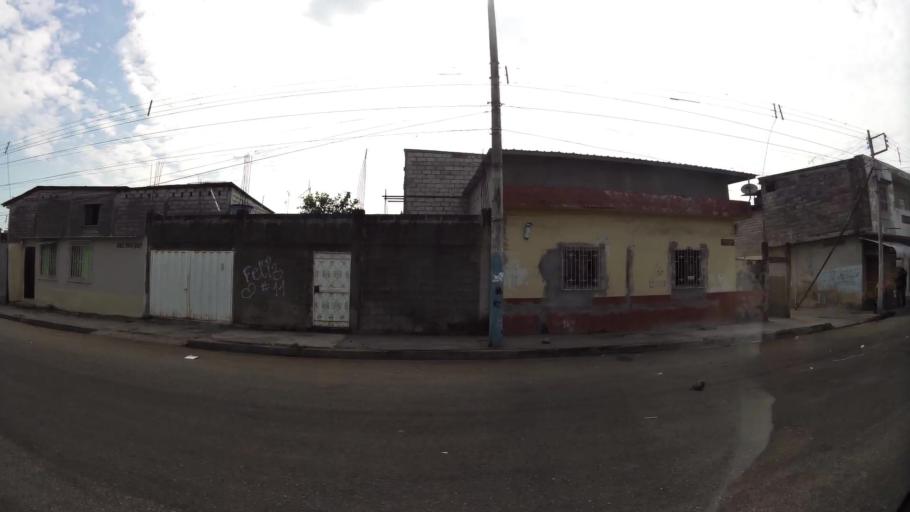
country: EC
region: Guayas
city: Guayaquil
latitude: -2.2503
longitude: -79.8816
